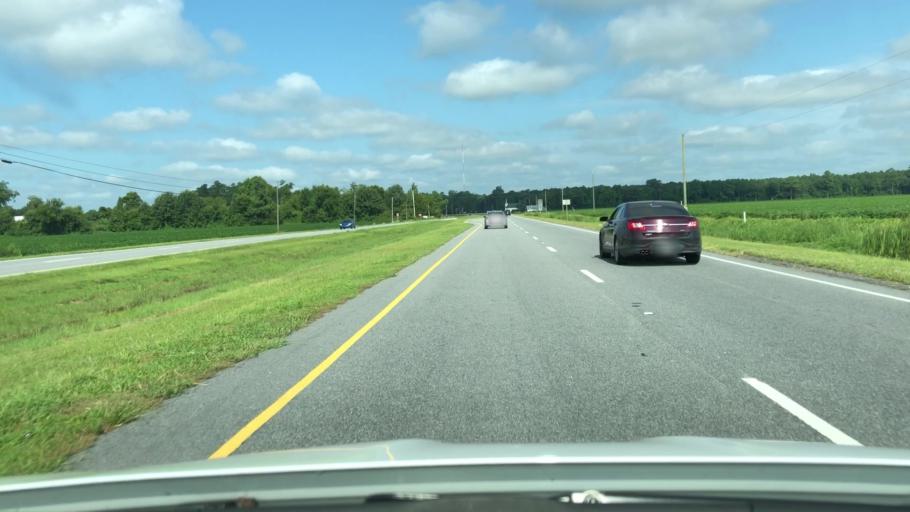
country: US
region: North Carolina
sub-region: Perquimans County
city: Hertford
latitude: 36.2104
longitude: -76.4217
